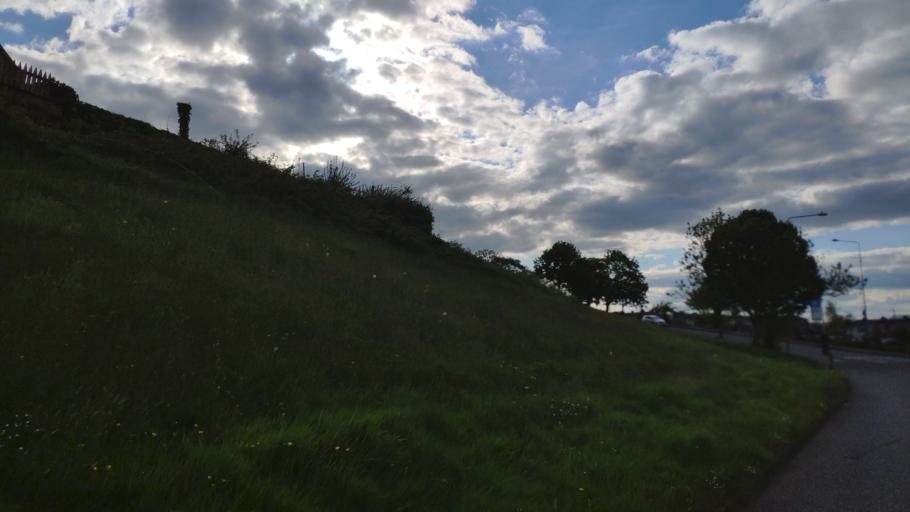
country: IE
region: Munster
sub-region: County Cork
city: Cork
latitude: 51.9110
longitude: -8.4586
